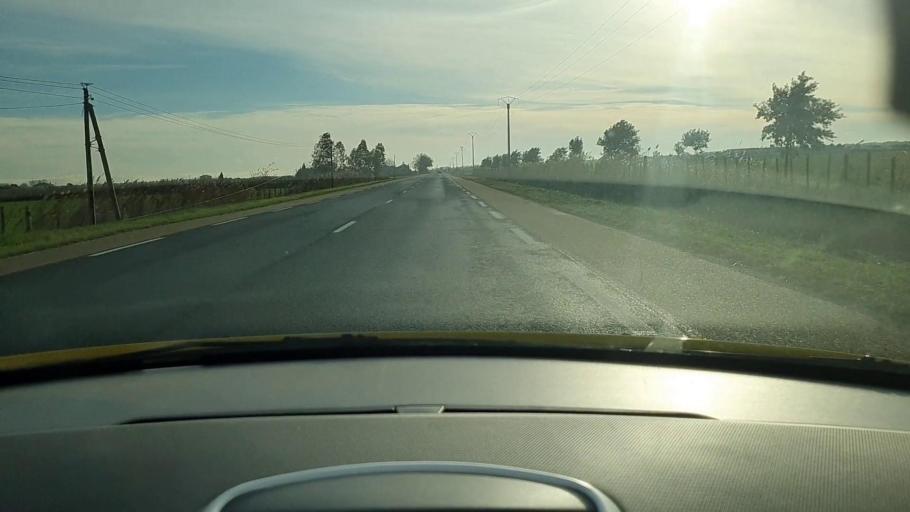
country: FR
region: Languedoc-Roussillon
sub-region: Departement du Gard
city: Bellegarde
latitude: 43.7274
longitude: 4.5364
